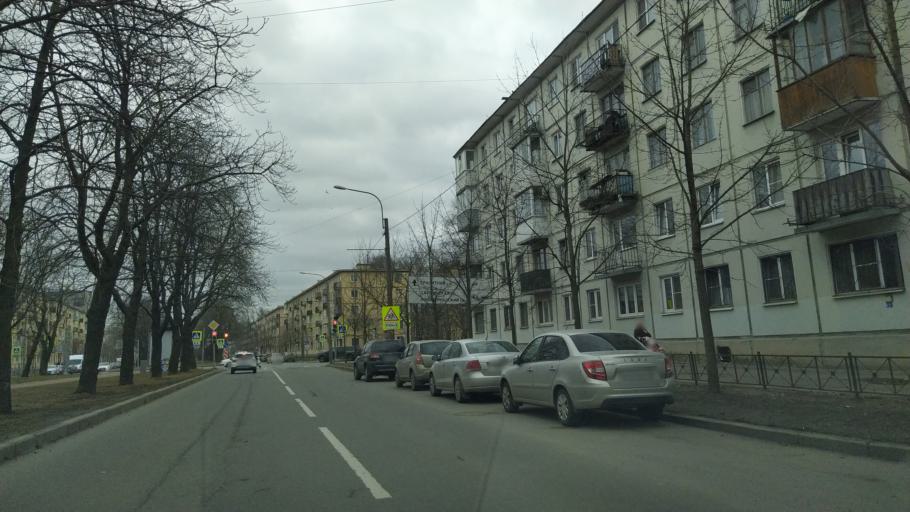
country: RU
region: St.-Petersburg
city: Centralniy
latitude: 59.9272
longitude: 30.4205
